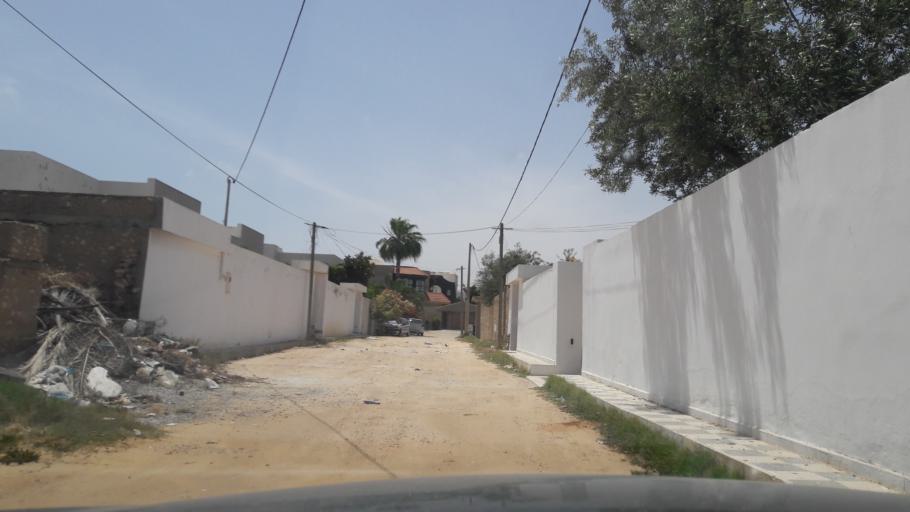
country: TN
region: Safaqis
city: Sfax
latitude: 34.7779
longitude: 10.7567
